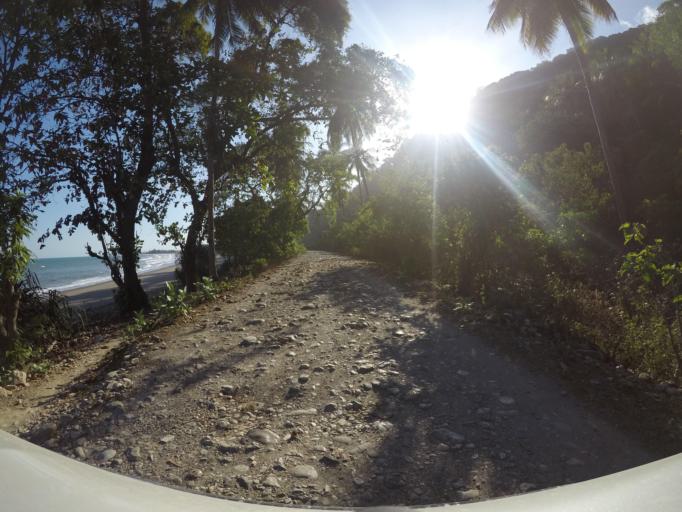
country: TL
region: Viqueque
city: Viqueque
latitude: -8.7998
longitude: 126.5903
